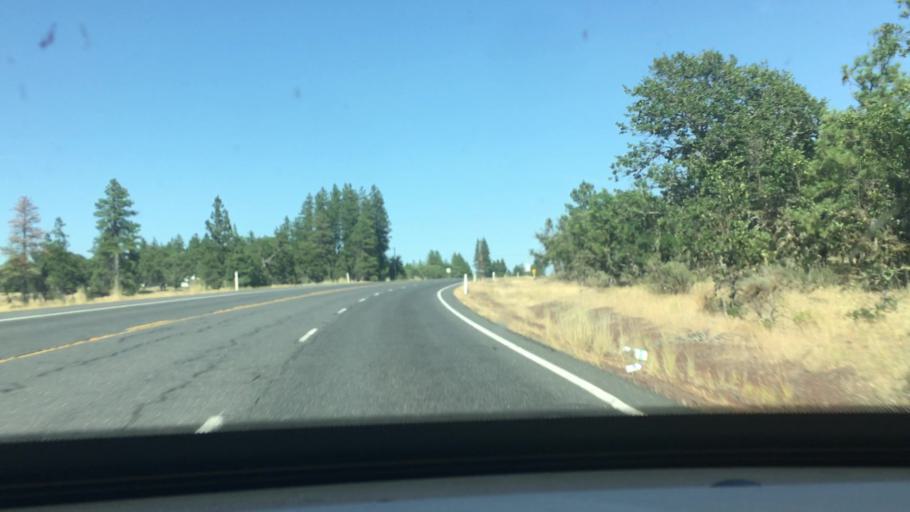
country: US
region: Washington
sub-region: Klickitat County
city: Goldendale
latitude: 45.8968
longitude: -120.7208
